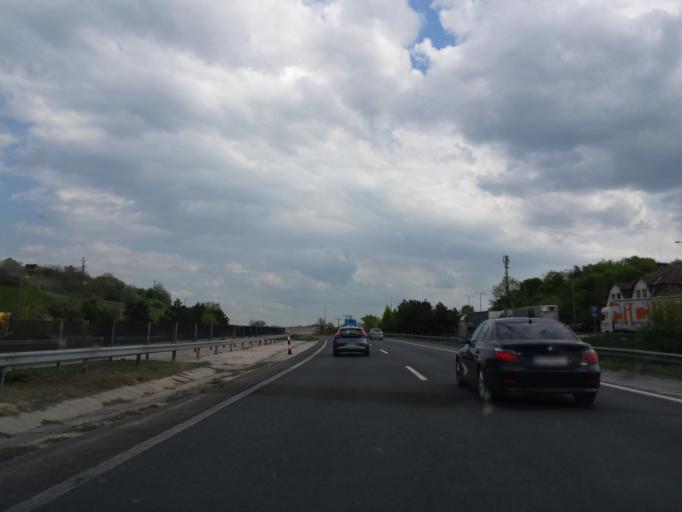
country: HU
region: Komarom-Esztergom
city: Tatabanya
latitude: 47.5790
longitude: 18.4129
